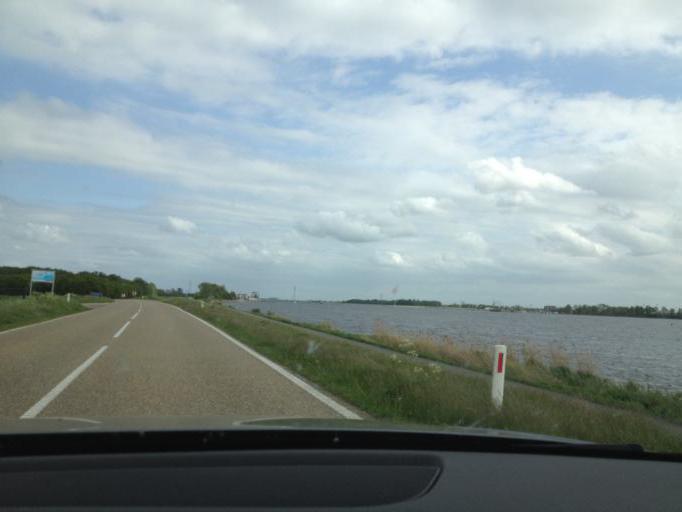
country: NL
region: Utrecht
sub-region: Gemeente Bunschoten
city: Spakenburg
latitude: 52.2691
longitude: 5.3771
